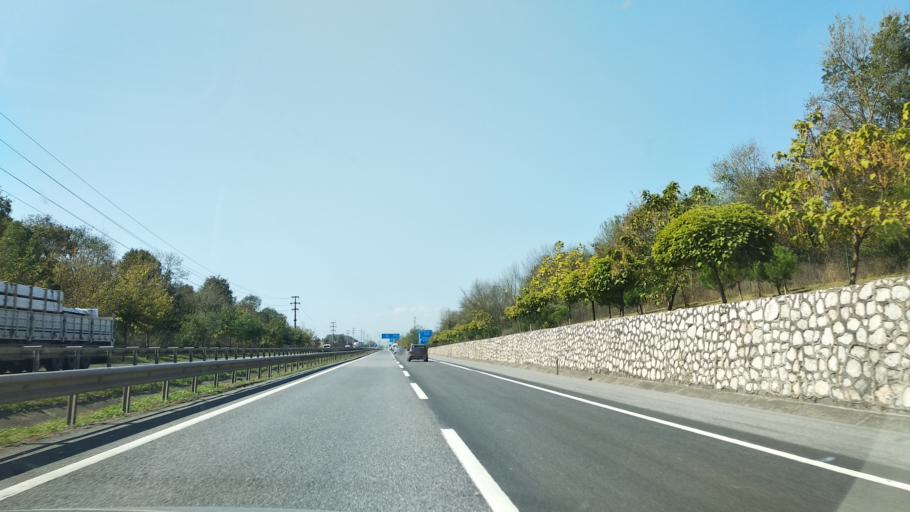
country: TR
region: Kocaeli
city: Derbent
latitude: 40.7418
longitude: 30.0885
